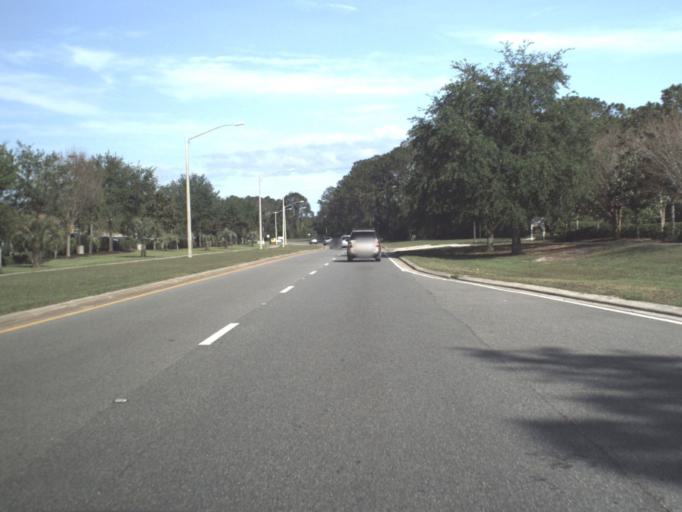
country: US
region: Florida
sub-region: Flagler County
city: Palm Coast
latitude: 29.5523
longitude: -81.2502
